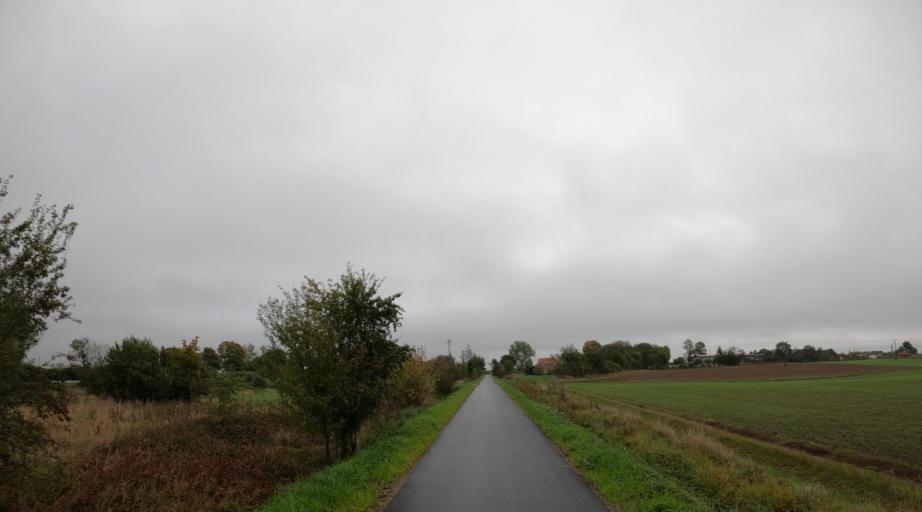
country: PL
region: West Pomeranian Voivodeship
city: Trzcinsko Zdroj
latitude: 52.9766
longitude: 14.6666
